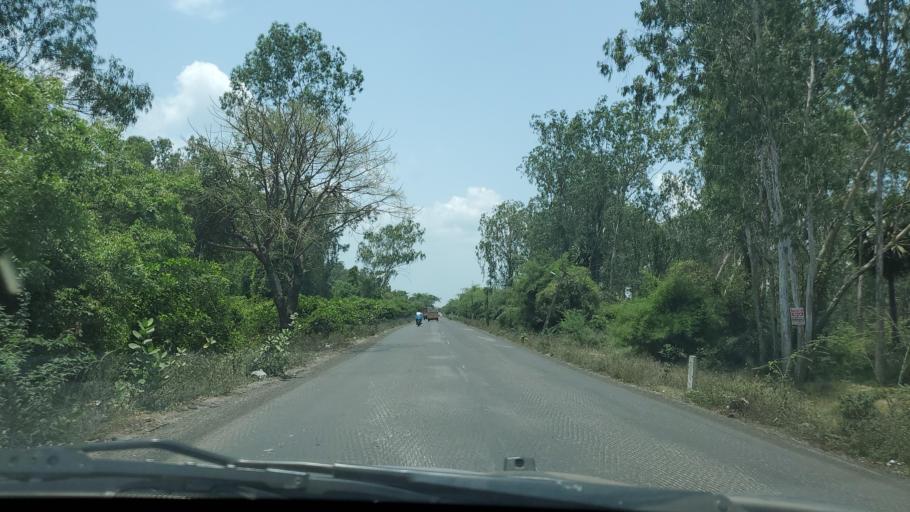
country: IN
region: Tamil Nadu
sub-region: Kancheepuram
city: Vengavasal
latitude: 12.8703
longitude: 80.1745
